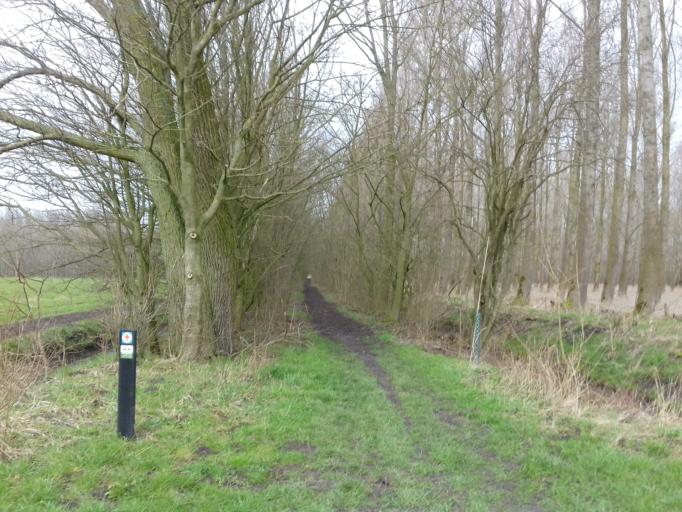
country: NL
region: Gelderland
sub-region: Gemeente Culemborg
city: Culemborg
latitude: 51.9123
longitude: 5.2176
